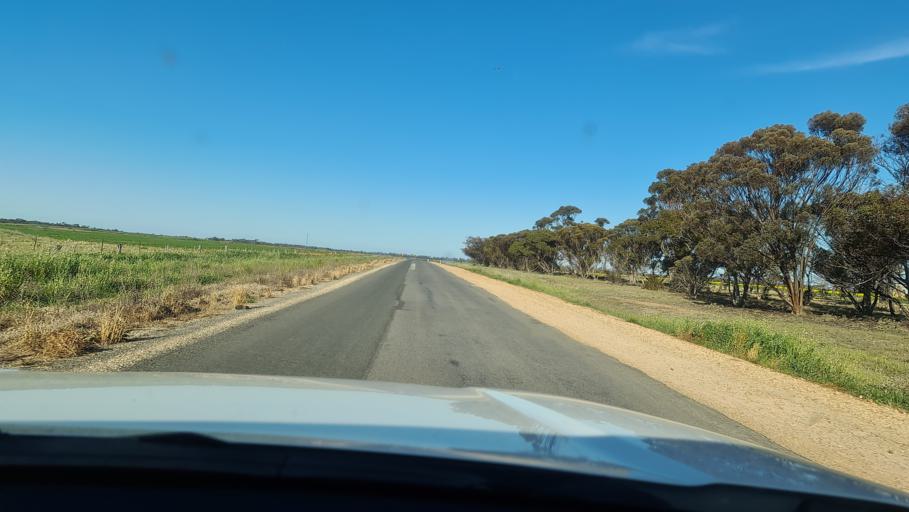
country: AU
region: Victoria
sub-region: Horsham
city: Horsham
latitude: -36.4492
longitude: 142.5661
